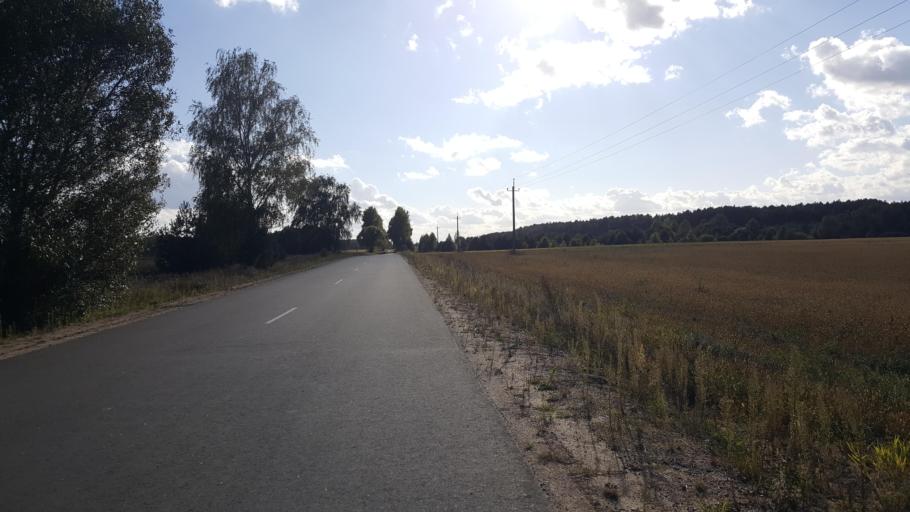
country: BY
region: Brest
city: Kamyanyets
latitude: 52.4137
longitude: 23.9201
